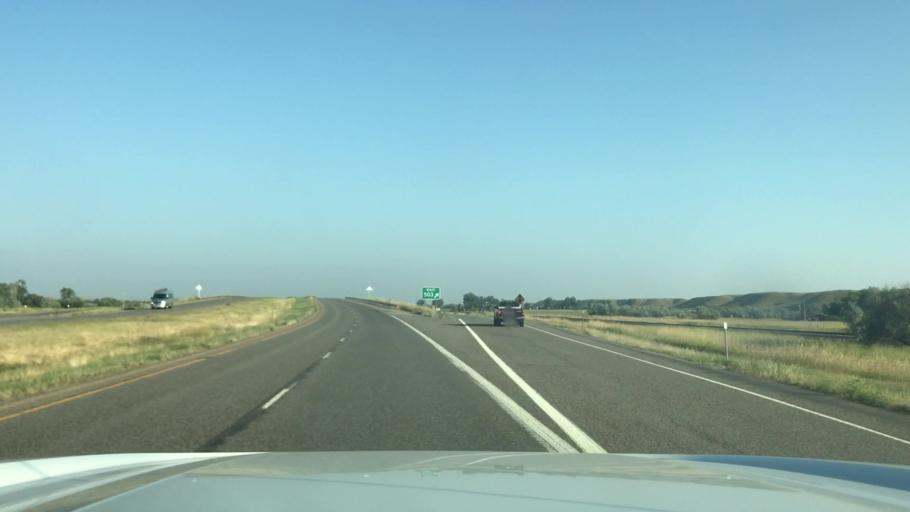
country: US
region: Montana
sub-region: Big Horn County
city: Crow Agency
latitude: 45.6831
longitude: -107.5078
